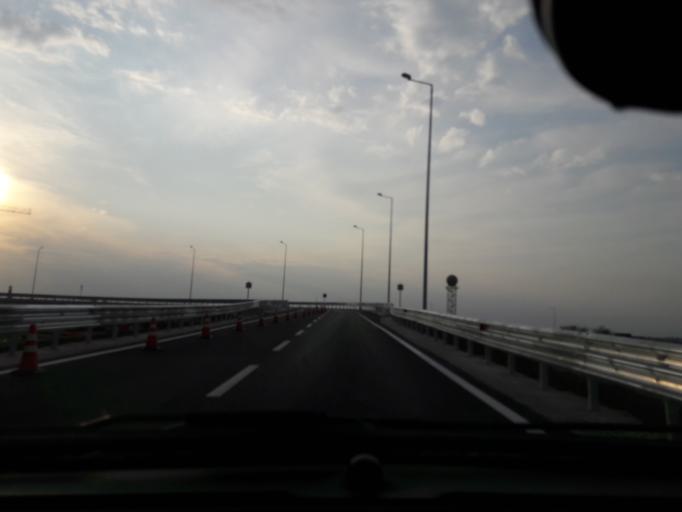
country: GR
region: Central Macedonia
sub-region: Nomos Thessalonikis
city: Neo Rysi
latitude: 40.5265
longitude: 22.9780
